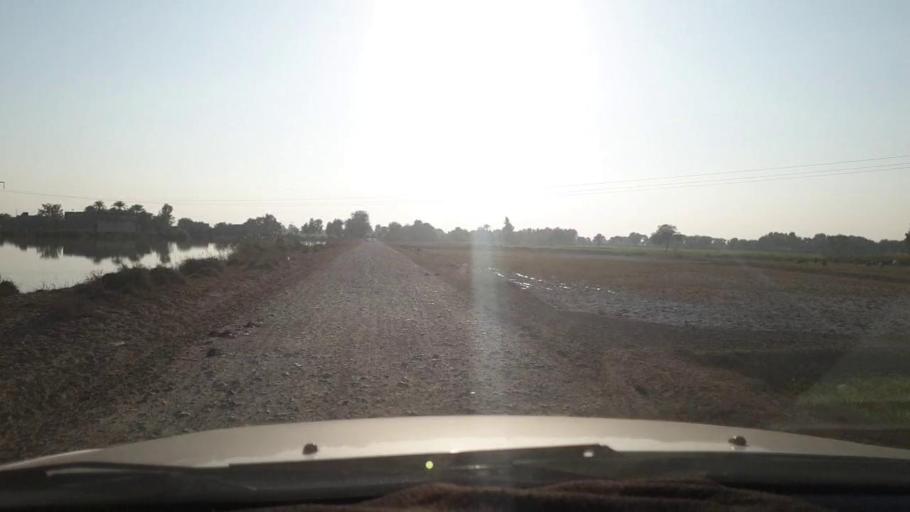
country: PK
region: Sindh
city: Mirpur Mathelo
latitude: 27.9999
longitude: 69.5253
